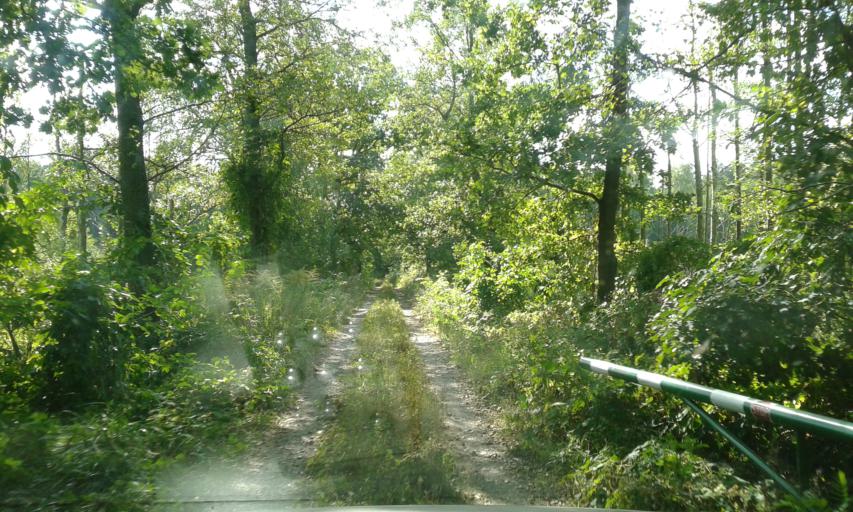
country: PL
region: West Pomeranian Voivodeship
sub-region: Powiat stargardzki
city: Suchan
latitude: 53.2081
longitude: 15.3184
